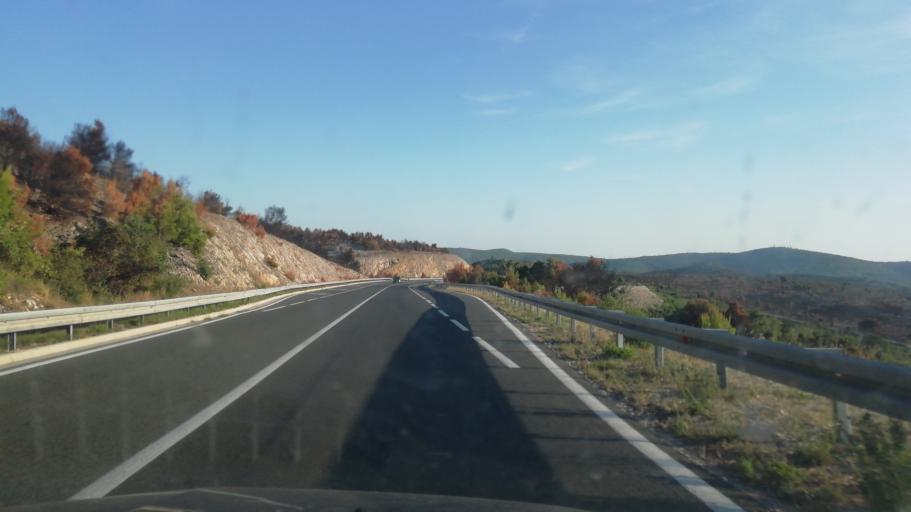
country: HR
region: Sibensko-Kniniska
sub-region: Grad Sibenik
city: Sibenik
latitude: 43.7661
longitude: 15.9380
